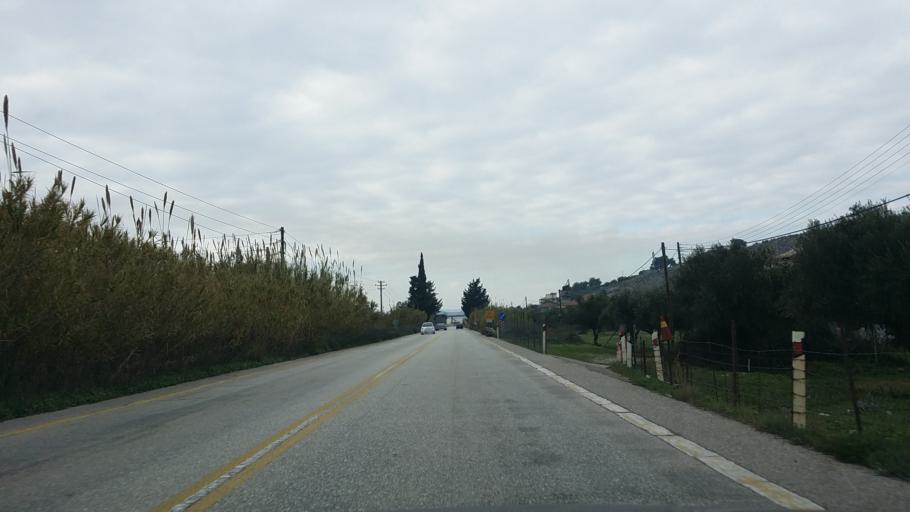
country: GR
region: West Greece
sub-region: Nomos Aitolias kai Akarnanias
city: Mesolongi
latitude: 38.3953
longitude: 21.4231
